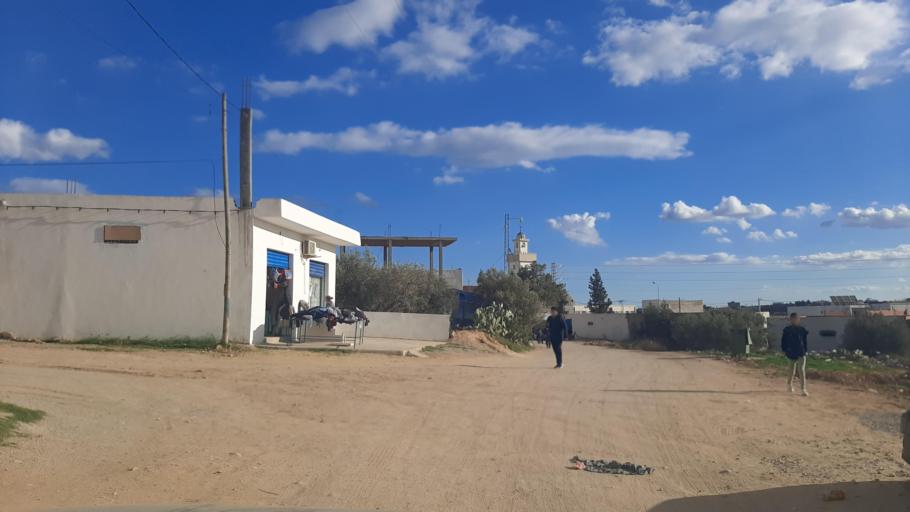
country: TN
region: Nabul
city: Al Hammamat
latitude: 36.4178
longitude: 10.5147
